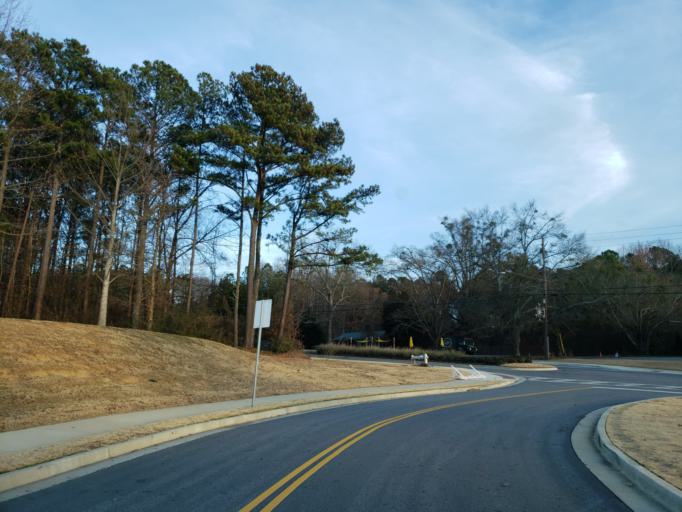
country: US
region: Georgia
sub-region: Cobb County
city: Kennesaw
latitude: 34.0211
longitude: -84.6199
